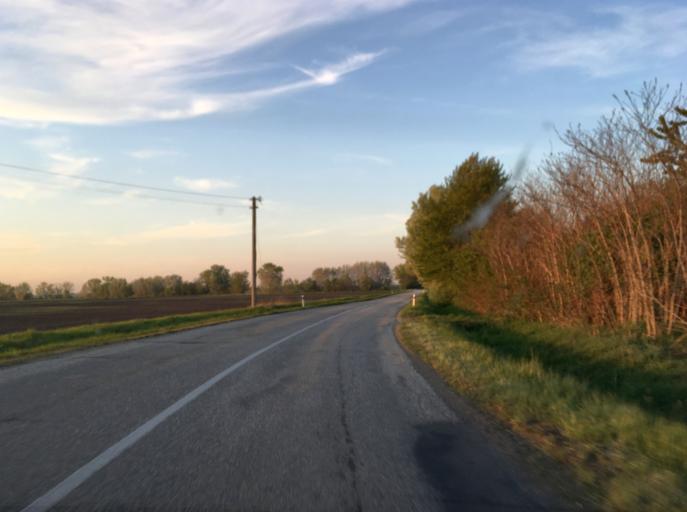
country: SK
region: Nitriansky
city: Kolarovo
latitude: 47.8935
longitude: 17.9218
